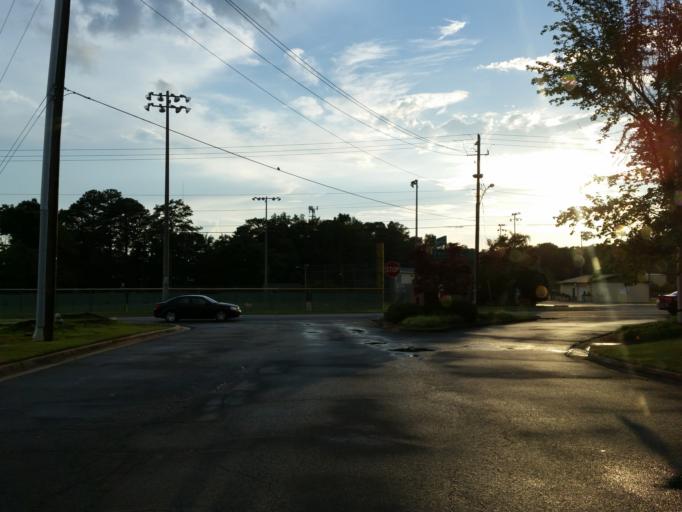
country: US
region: Georgia
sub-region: Cobb County
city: Marietta
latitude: 33.9395
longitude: -84.5346
